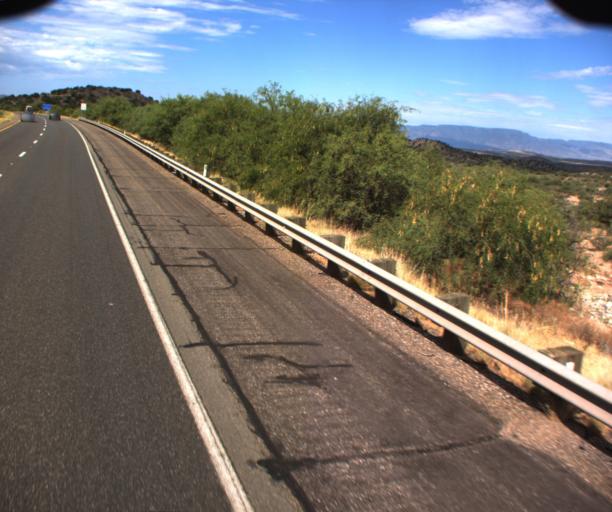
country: US
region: Arizona
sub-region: Yavapai County
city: Lake Montezuma
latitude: 34.6827
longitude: -111.7506
